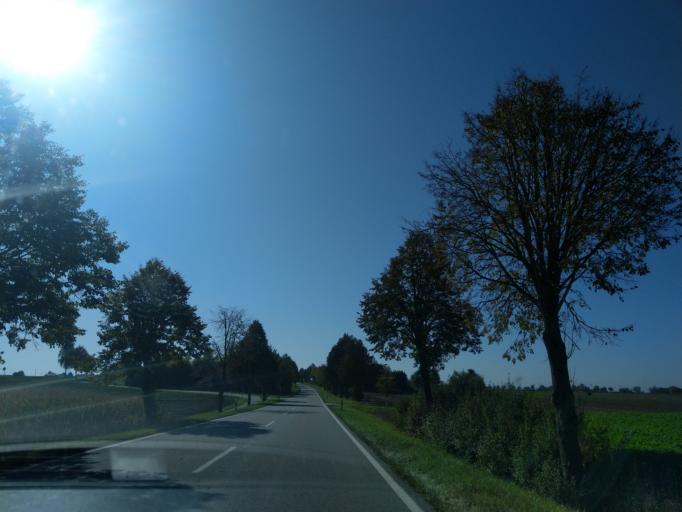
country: DE
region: Bavaria
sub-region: Lower Bavaria
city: Stephansposching
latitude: 48.8122
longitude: 12.8012
